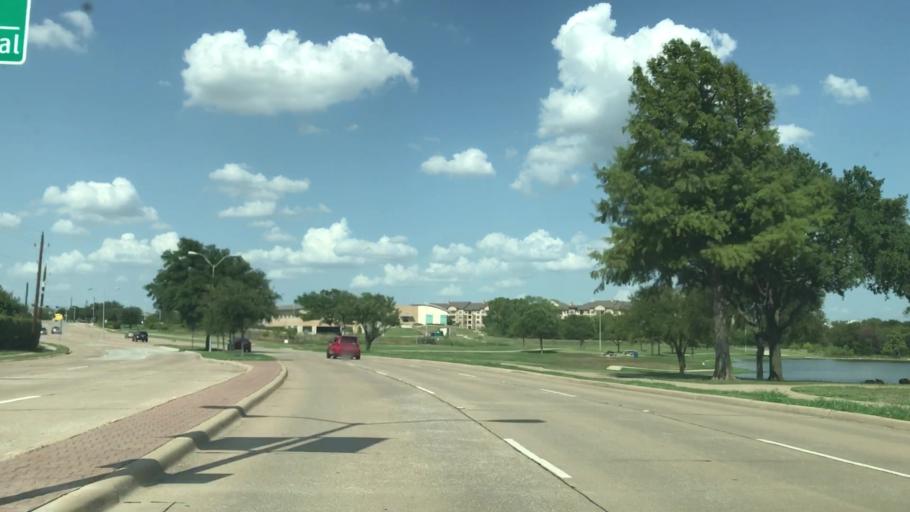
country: US
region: Texas
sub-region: Dallas County
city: Carrollton
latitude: 32.9688
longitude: -96.8963
